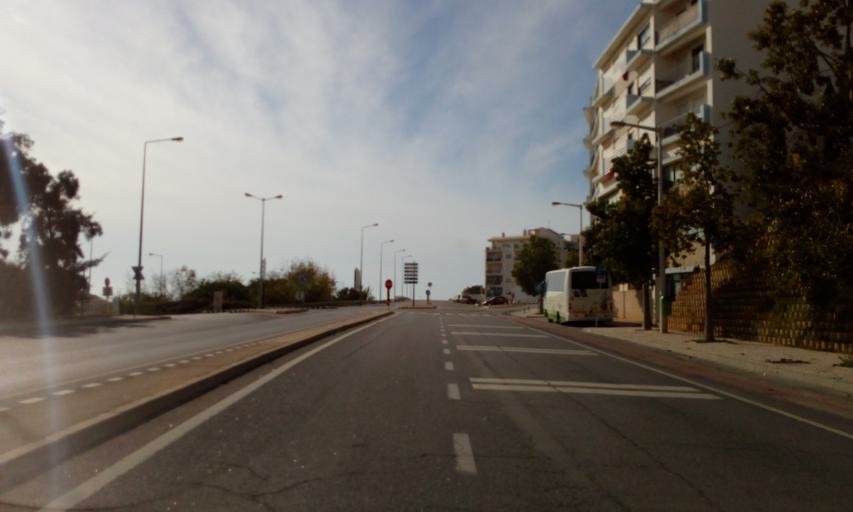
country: PT
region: Faro
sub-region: Faro
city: Faro
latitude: 37.0166
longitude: -7.9153
